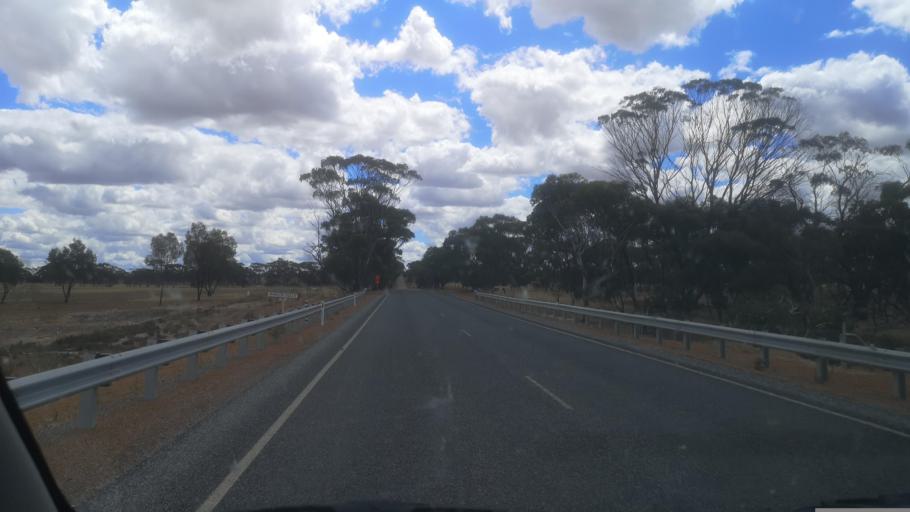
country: AU
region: Western Australia
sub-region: Beverley
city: Beverley
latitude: -31.9899
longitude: 117.1258
